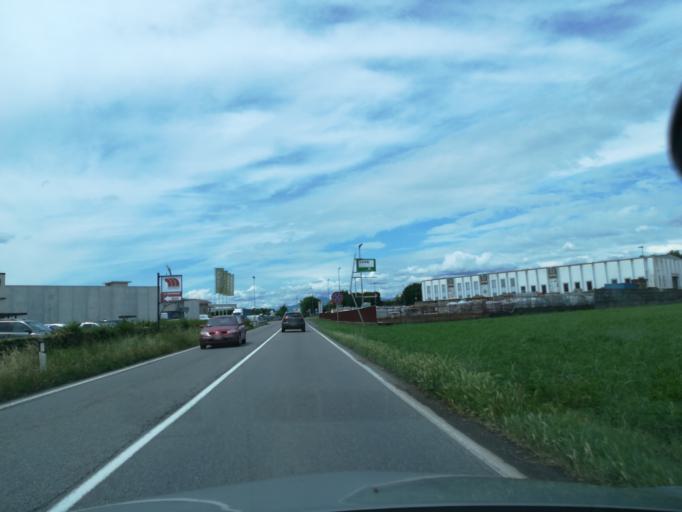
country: IT
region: Lombardy
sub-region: Provincia di Bergamo
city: Mornico al Serio
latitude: 45.5986
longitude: 9.8144
